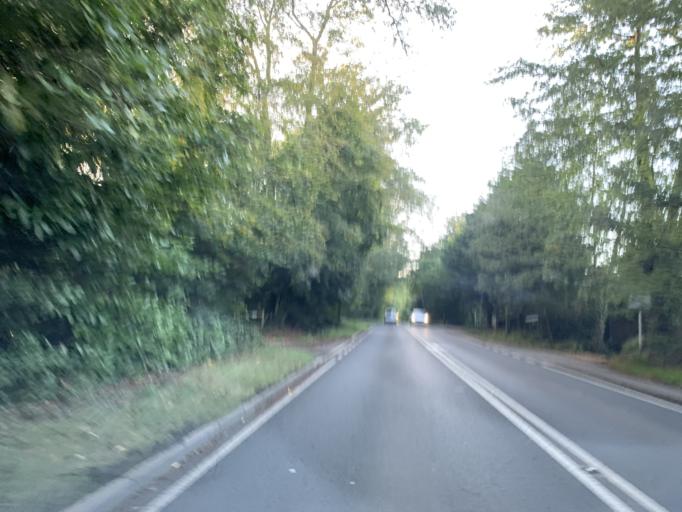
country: GB
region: England
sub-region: Hampshire
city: West Wellow
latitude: 50.9659
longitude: -1.5757
